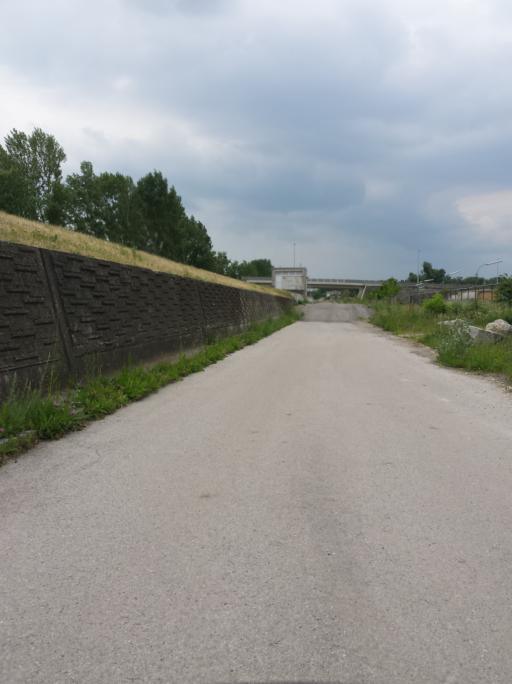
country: AT
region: Lower Austria
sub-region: Politischer Bezirk Wien-Umgebung
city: Schwechat
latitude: 48.1768
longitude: 16.4666
